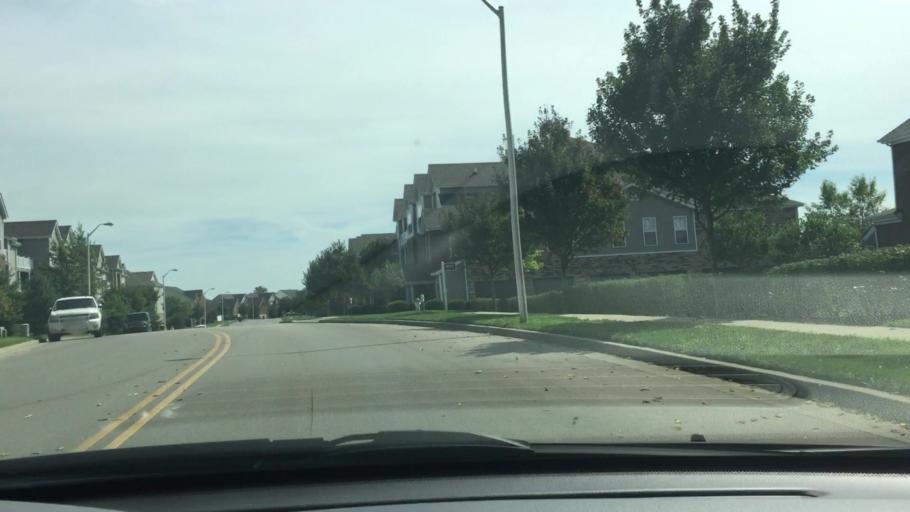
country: US
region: Kentucky
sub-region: Fayette County
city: Monticello
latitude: 37.9690
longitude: -84.5219
